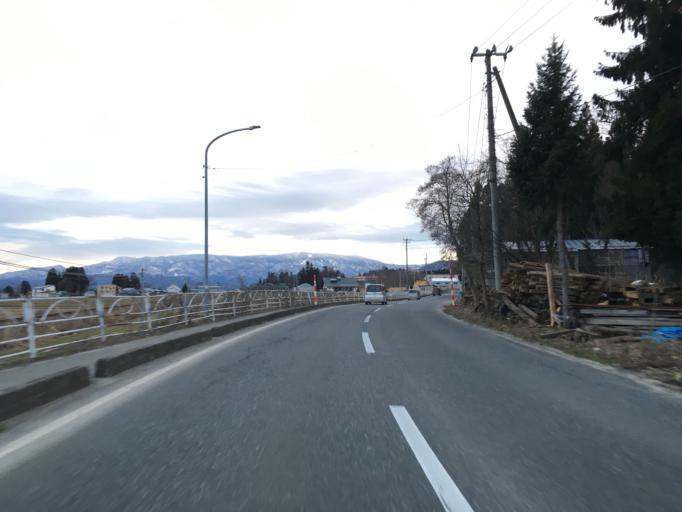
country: JP
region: Yamagata
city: Yonezawa
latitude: 37.9414
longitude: 140.0762
